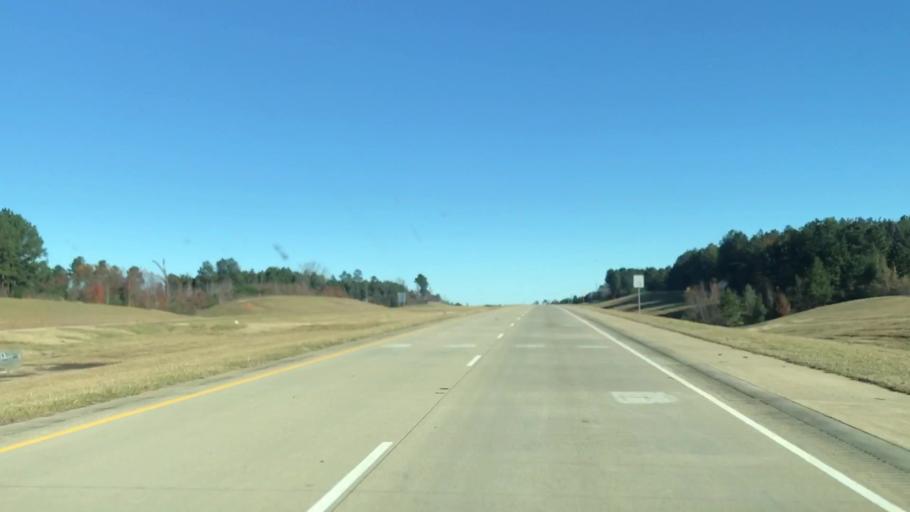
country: US
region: Louisiana
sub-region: Caddo Parish
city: Vivian
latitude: 33.0080
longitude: -93.9050
